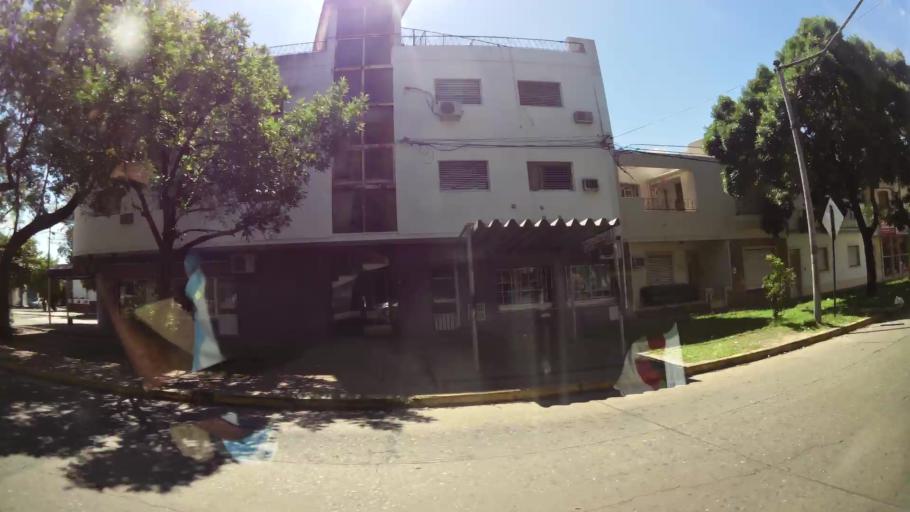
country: AR
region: Santa Fe
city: Santa Fe de la Vera Cruz
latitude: -31.6306
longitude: -60.6933
